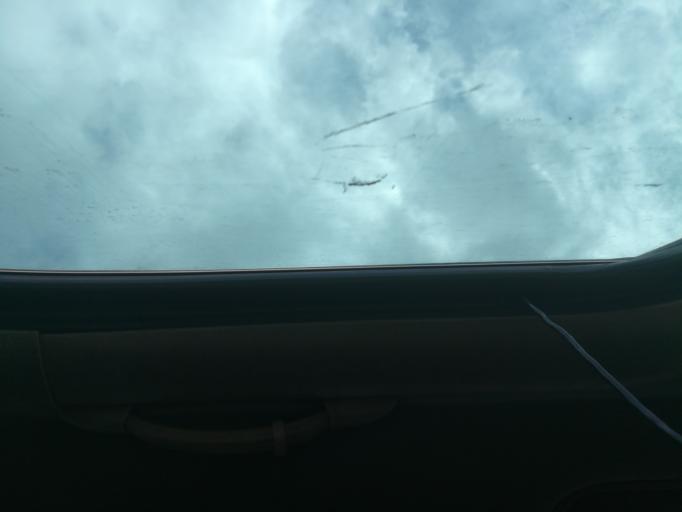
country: NG
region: Lagos
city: Lagos
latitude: 6.4144
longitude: 3.4136
